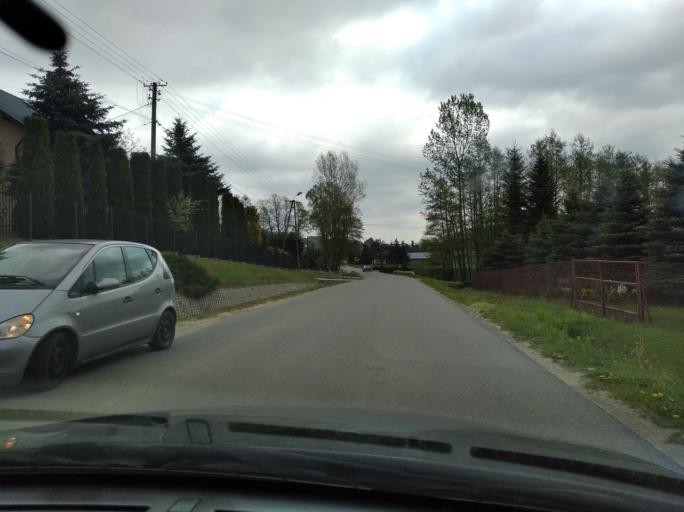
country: PL
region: Subcarpathian Voivodeship
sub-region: Powiat debicki
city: Leki Dolne
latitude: 49.9770
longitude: 21.2263
